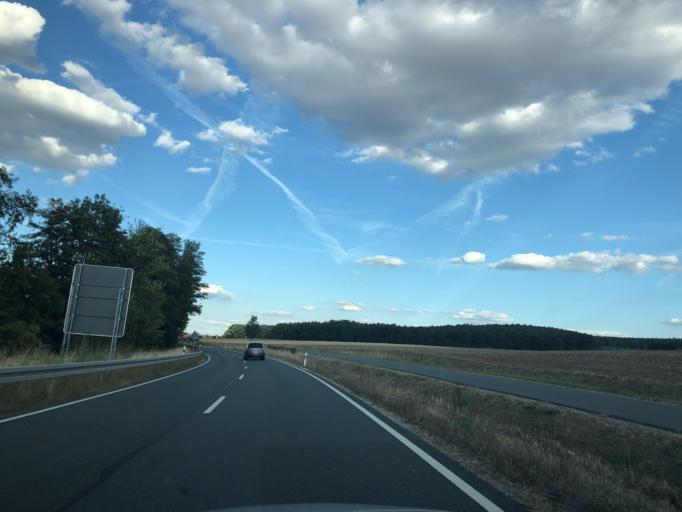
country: DE
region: Bavaria
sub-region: Upper Franconia
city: Burgebrach
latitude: 49.8248
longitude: 10.7128
